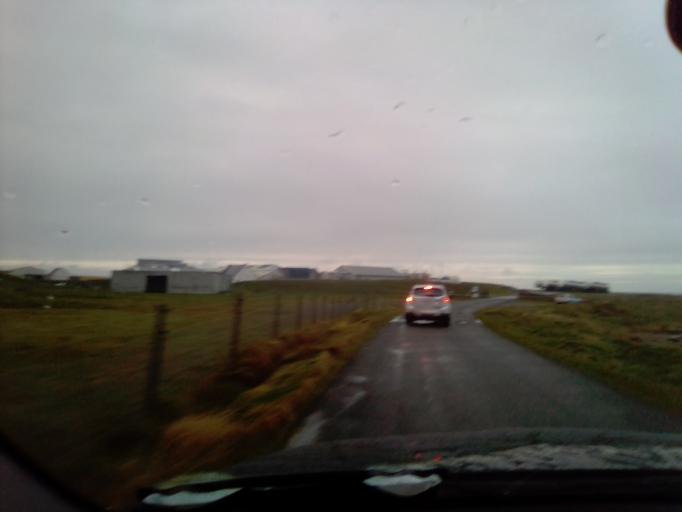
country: IE
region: Ulster
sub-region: County Donegal
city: Ramelton
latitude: 55.2619
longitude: -7.6875
